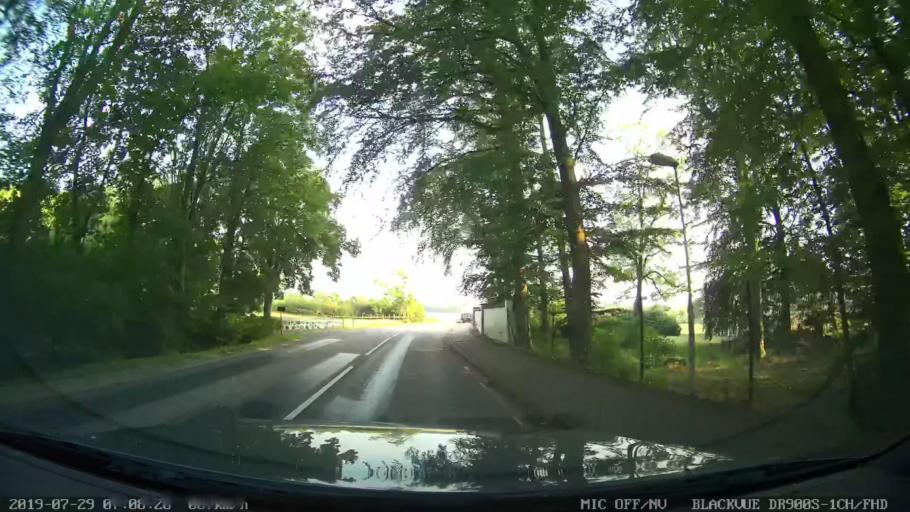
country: SE
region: Skane
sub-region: Helsingborg
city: Odakra
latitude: 56.0989
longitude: 12.6988
